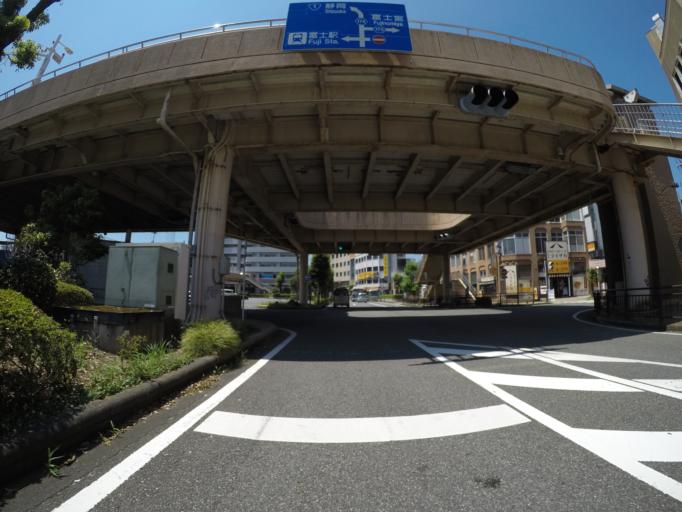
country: JP
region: Shizuoka
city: Fuji
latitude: 35.1521
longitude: 138.6511
